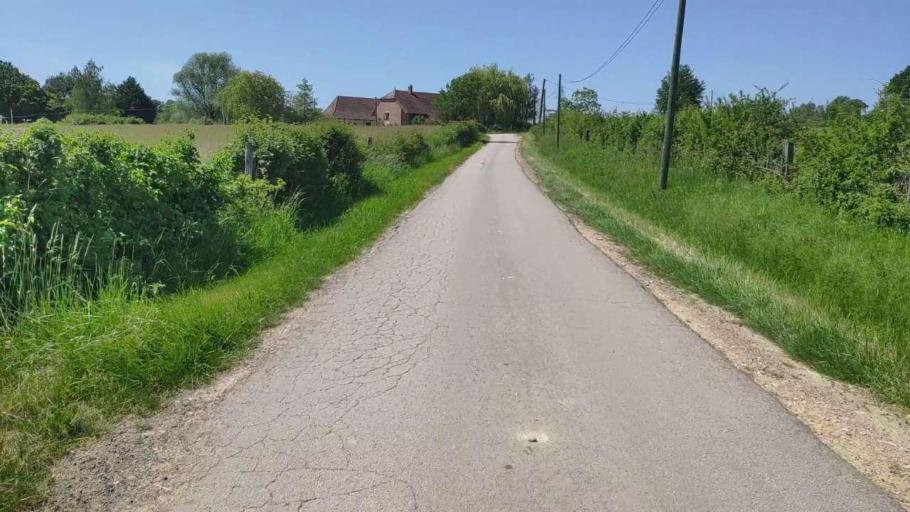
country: FR
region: Franche-Comte
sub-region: Departement du Jura
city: Bletterans
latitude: 46.7735
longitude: 5.4025
